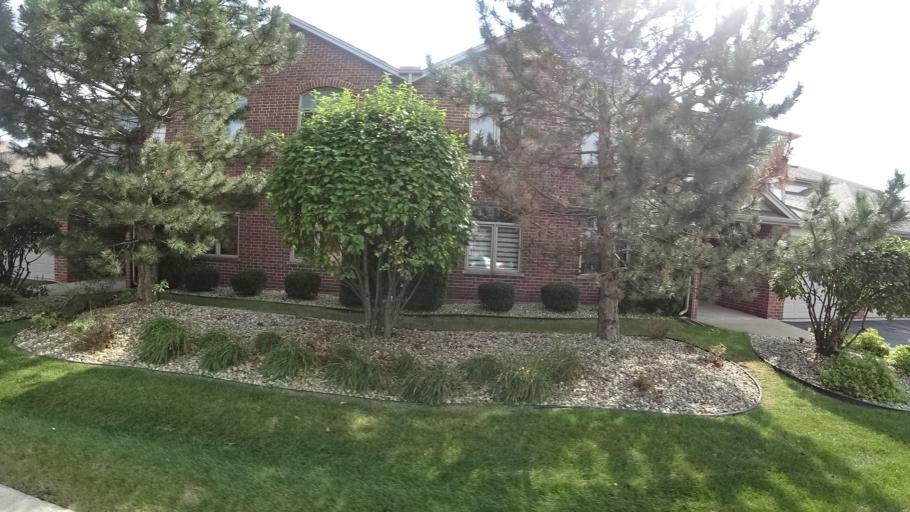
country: US
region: Illinois
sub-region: Cook County
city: Tinley Park
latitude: 41.5584
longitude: -87.7679
